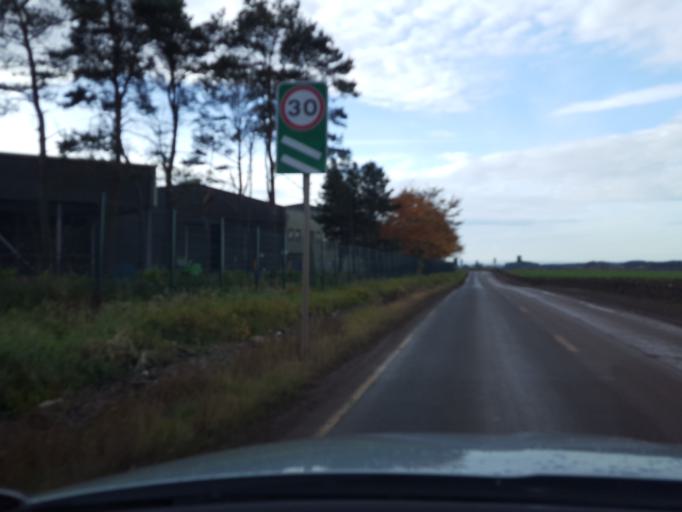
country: GB
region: Scotland
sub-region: South Lanarkshire
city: Carnwath
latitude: 55.7060
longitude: -3.6132
